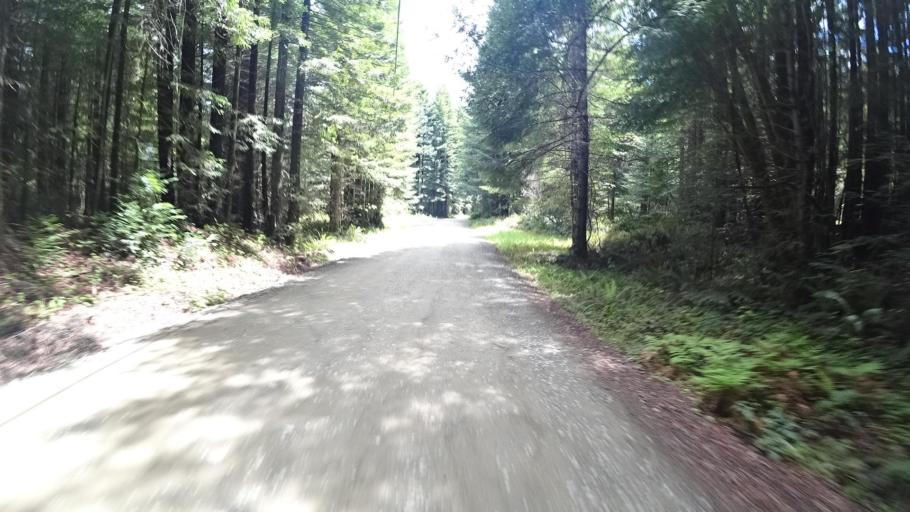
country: US
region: California
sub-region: Humboldt County
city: Blue Lake
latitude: 40.8057
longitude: -123.8832
